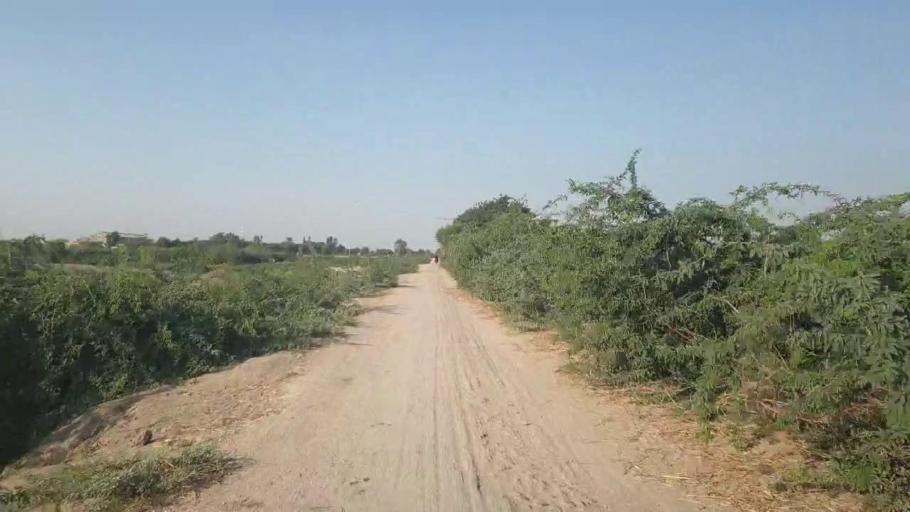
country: PK
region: Sindh
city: Badin
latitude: 24.6518
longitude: 68.8152
